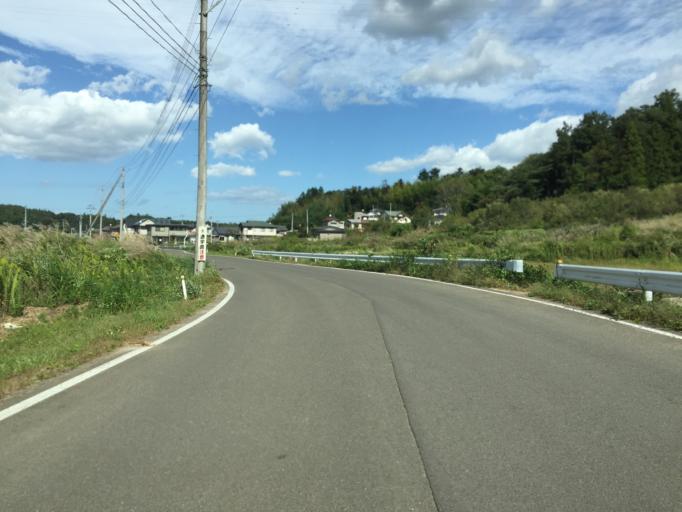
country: JP
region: Fukushima
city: Hobaramachi
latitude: 37.7801
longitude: 140.5492
